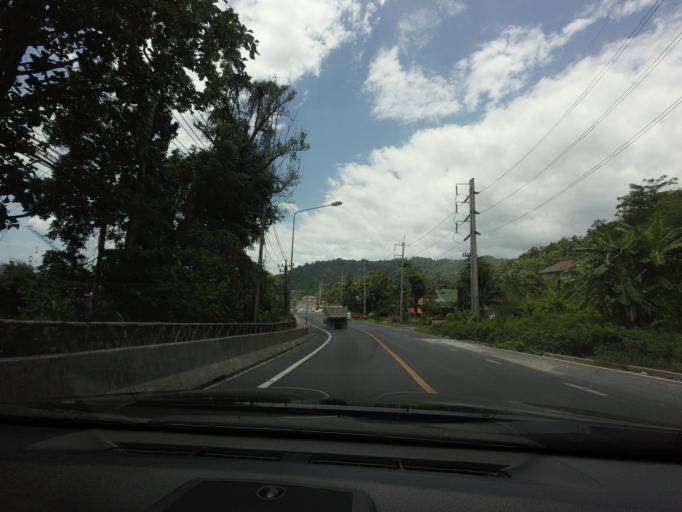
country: TH
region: Phangnga
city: Ban Khao Lak
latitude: 8.6365
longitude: 98.2474
